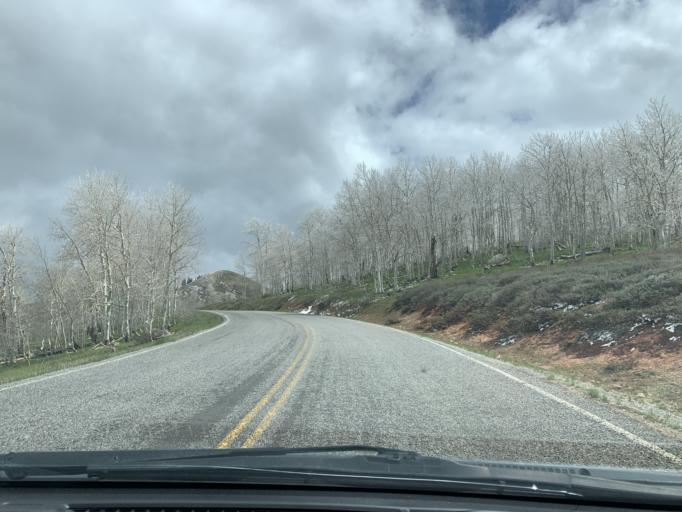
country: US
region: Utah
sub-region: Utah County
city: Santaquin
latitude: 39.8602
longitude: -111.6948
